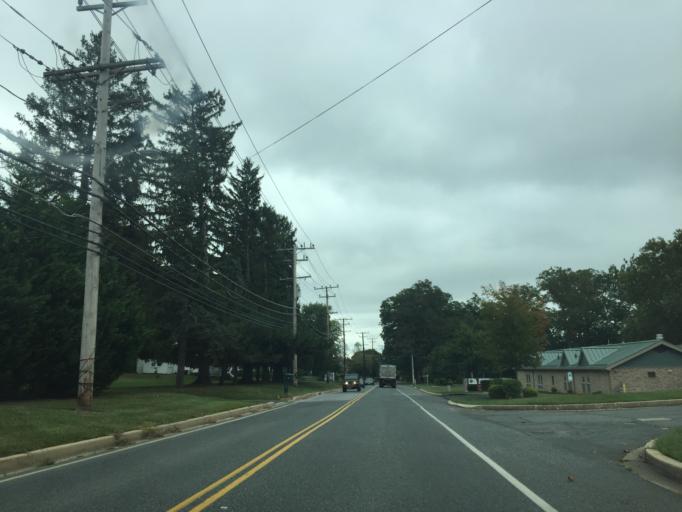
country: US
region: Maryland
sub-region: Harford County
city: Bel Air North
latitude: 39.5847
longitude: -76.3852
